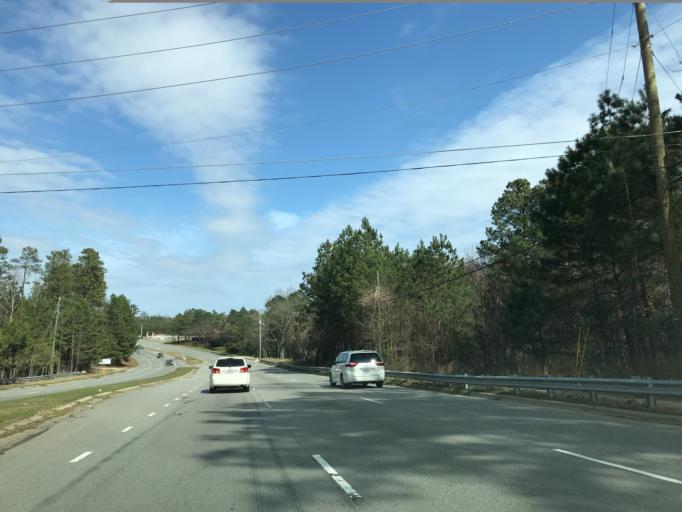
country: US
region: North Carolina
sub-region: Wake County
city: Raleigh
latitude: 35.8460
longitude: -78.5665
